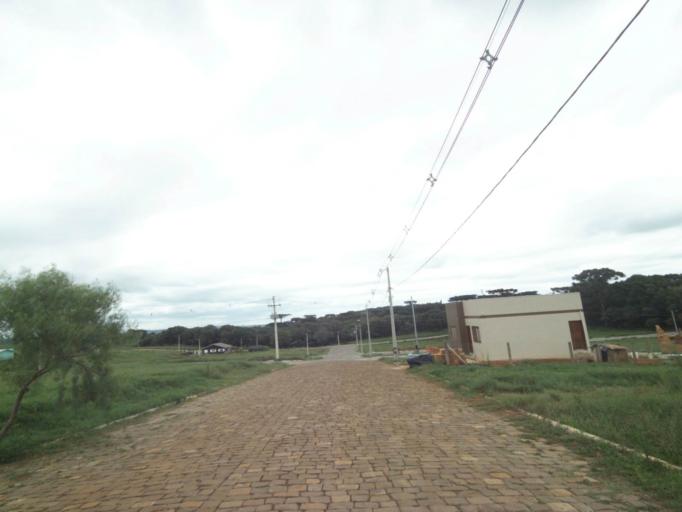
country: BR
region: Rio Grande do Sul
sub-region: Lagoa Vermelha
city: Lagoa Vermelha
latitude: -28.1882
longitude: -51.5272
